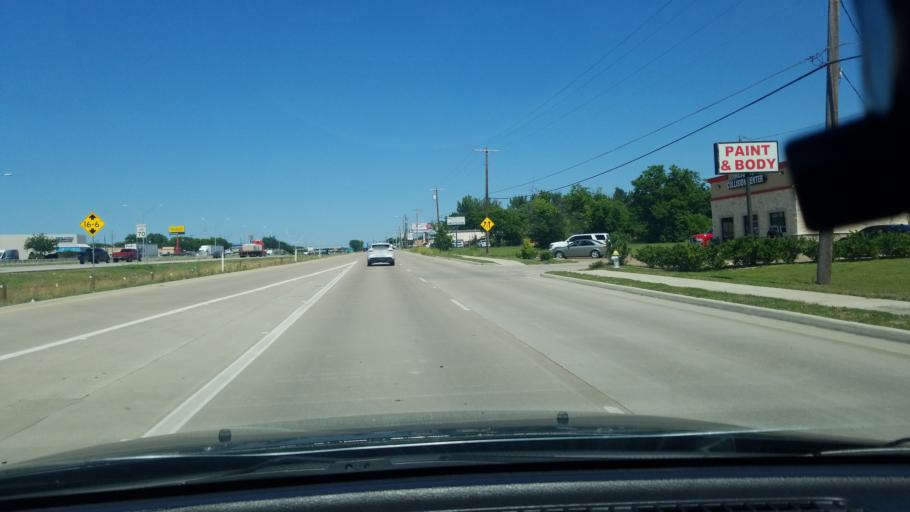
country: US
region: Texas
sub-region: Dallas County
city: Mesquite
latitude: 32.7923
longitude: -96.6184
